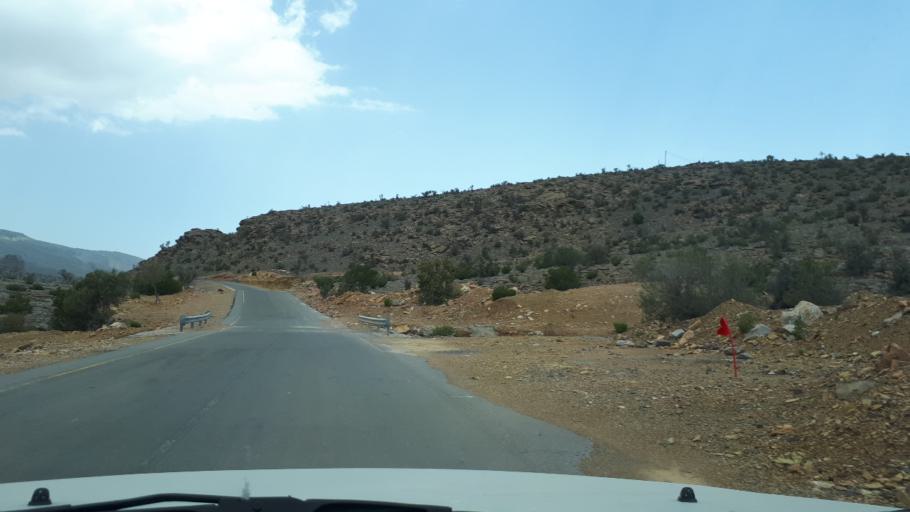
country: OM
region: Muhafazat ad Dakhiliyah
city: Bahla'
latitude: 23.2258
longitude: 57.2018
